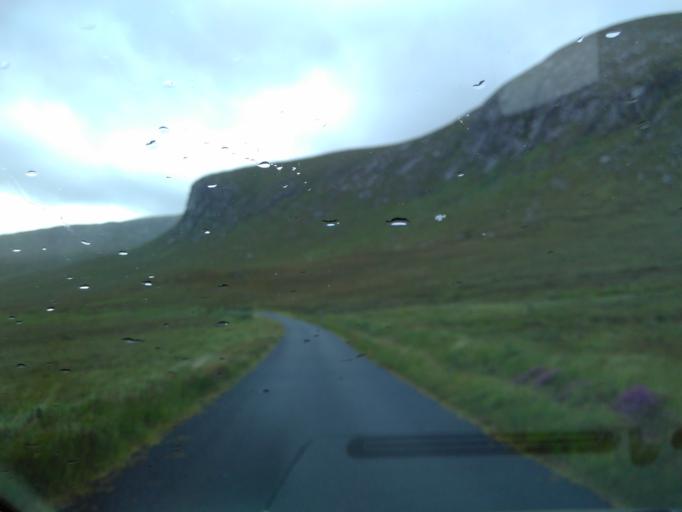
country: IE
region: Ulster
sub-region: County Donegal
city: Dunlewy
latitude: 54.9721
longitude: -8.0862
